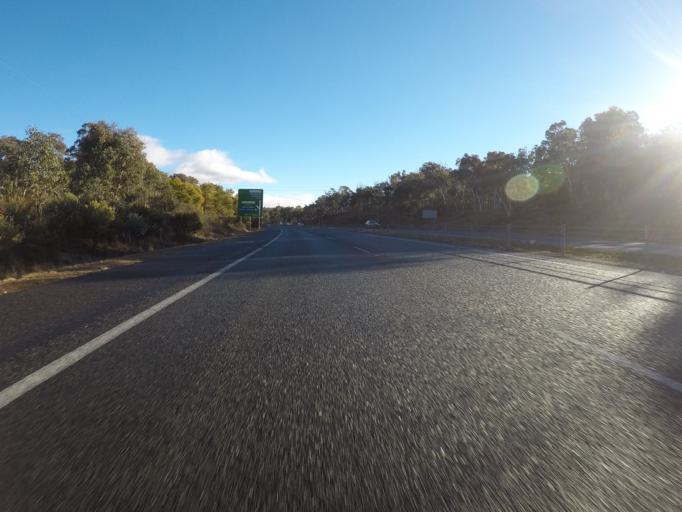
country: AU
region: Australian Capital Territory
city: Acton
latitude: -35.2717
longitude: 149.0881
